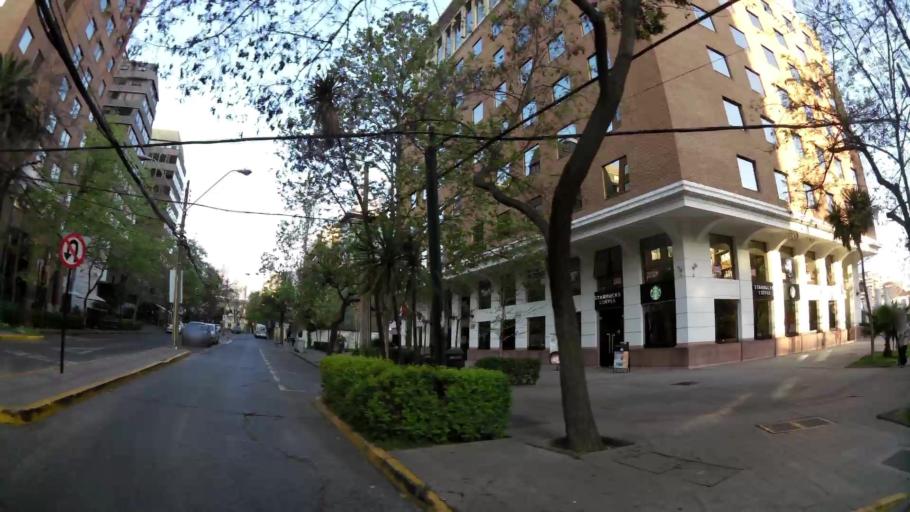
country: CL
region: Santiago Metropolitan
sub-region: Provincia de Santiago
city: Santiago
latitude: -33.4272
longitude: -70.6127
